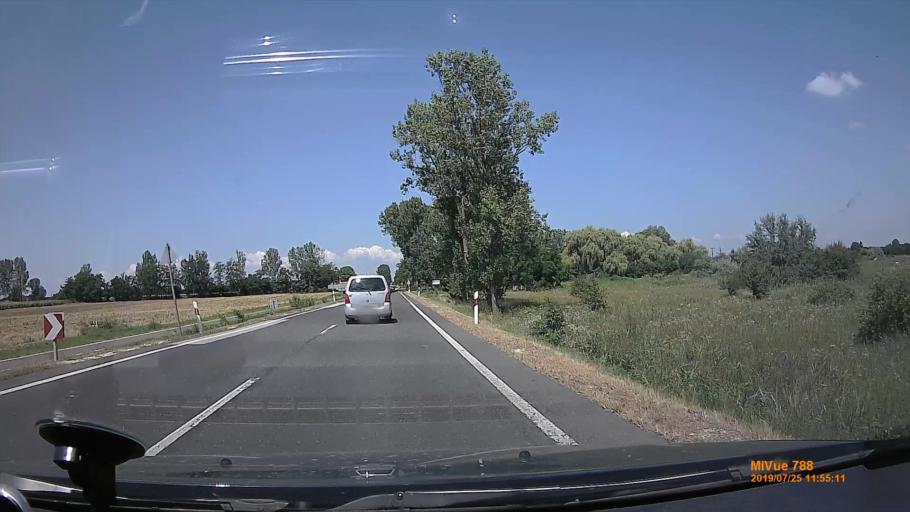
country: HU
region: Szabolcs-Szatmar-Bereg
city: Nyirtelek
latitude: 47.9961
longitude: 21.6519
